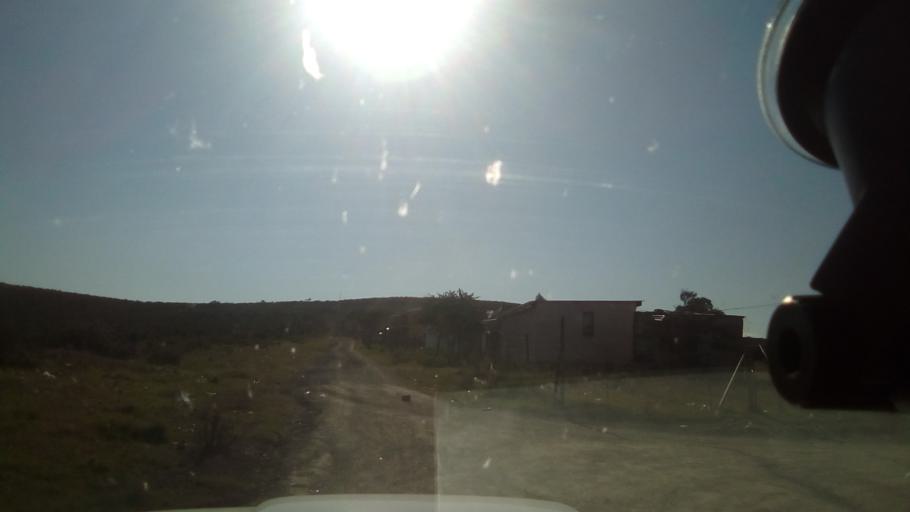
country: ZA
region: Eastern Cape
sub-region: Buffalo City Metropolitan Municipality
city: Bhisho
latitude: -32.8173
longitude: 27.3513
